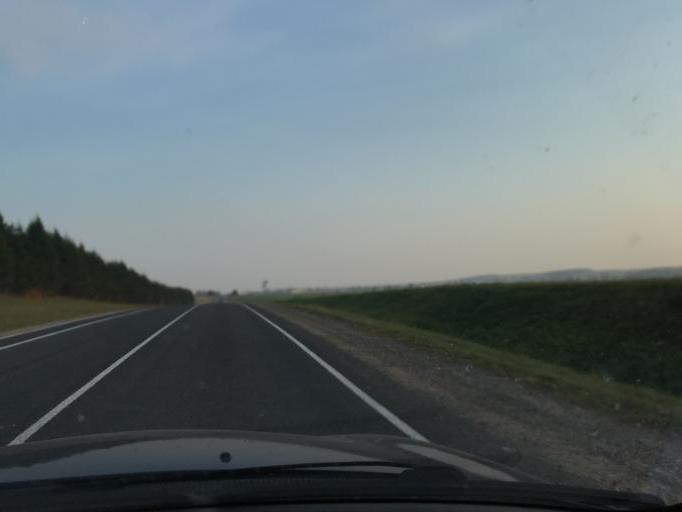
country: BY
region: Grodnenskaya
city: Karelichy
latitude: 53.5857
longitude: 26.1098
